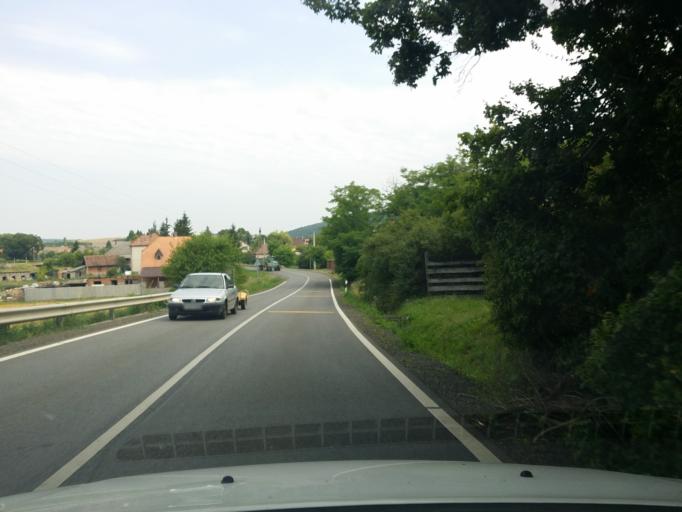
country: HU
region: Pest
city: Acsa
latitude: 47.7705
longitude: 19.3707
